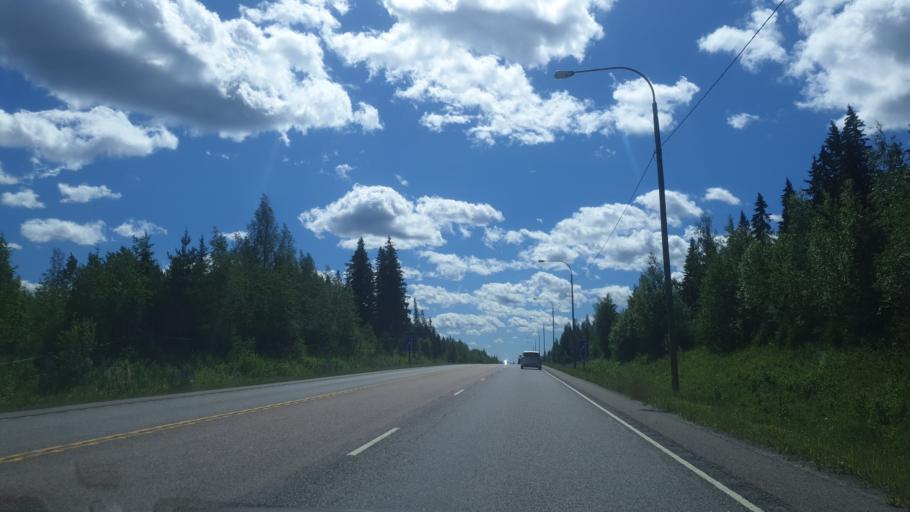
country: FI
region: Northern Savo
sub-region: Varkaus
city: Varkaus
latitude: 62.3729
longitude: 27.8096
